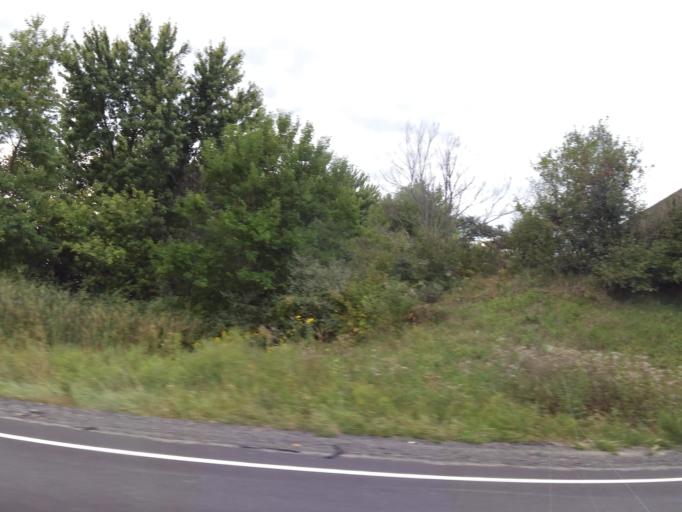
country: US
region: Indiana
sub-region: Lake County
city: Winfield
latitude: 41.3693
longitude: -87.3207
